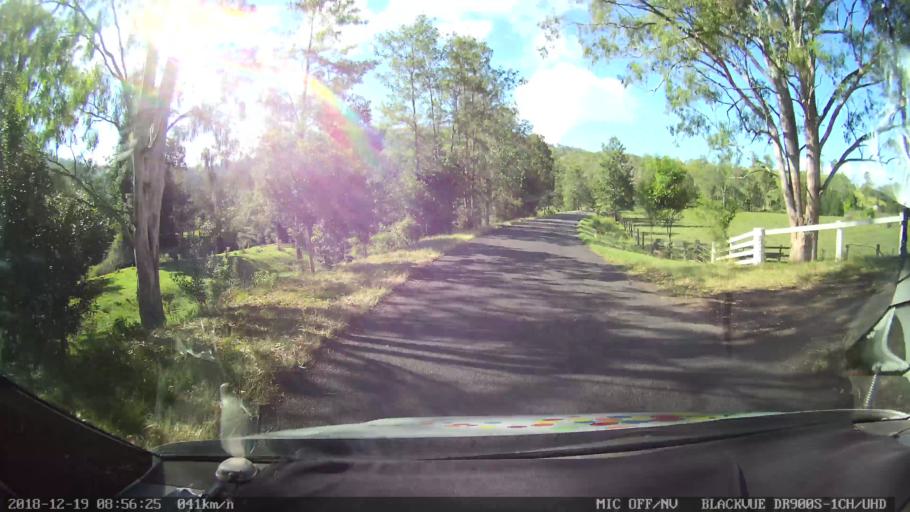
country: AU
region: New South Wales
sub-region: Kyogle
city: Kyogle
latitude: -28.4187
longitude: 152.9765
